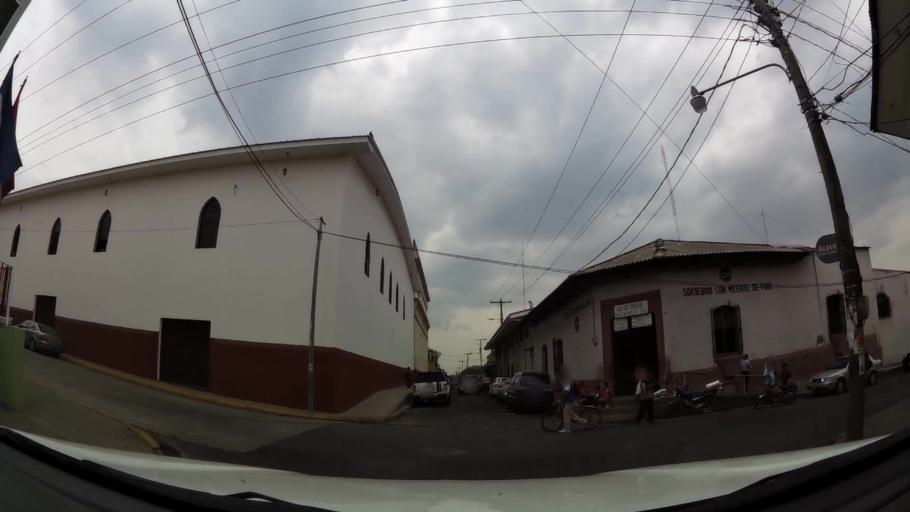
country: NI
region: Leon
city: Leon
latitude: 12.4337
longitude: -86.8794
